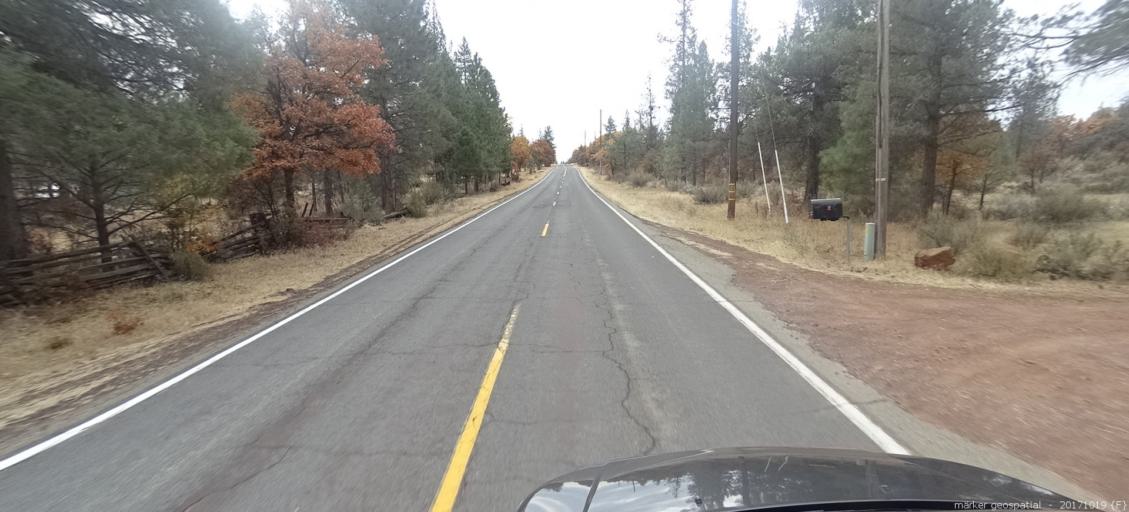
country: US
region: California
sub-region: Shasta County
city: Burney
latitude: 41.1105
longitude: -121.3299
